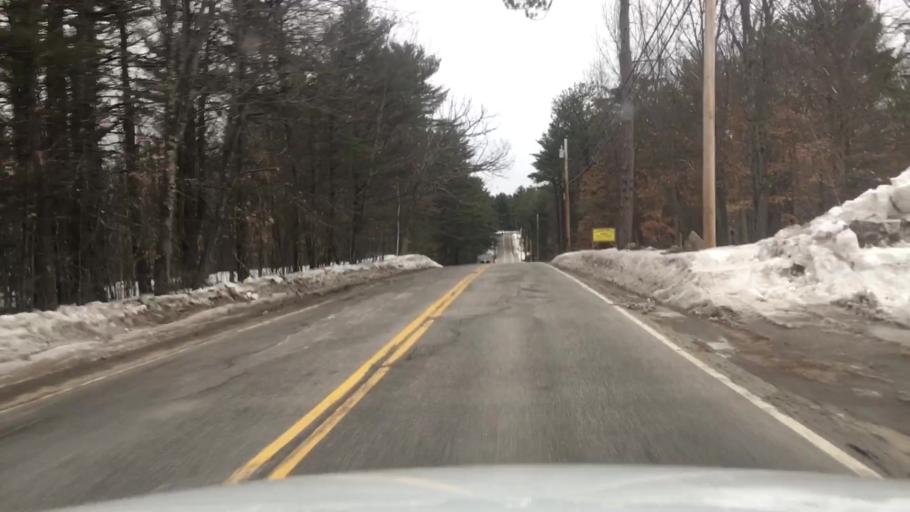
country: US
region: Maine
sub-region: York County
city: Shapleigh
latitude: 43.5540
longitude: -70.8550
